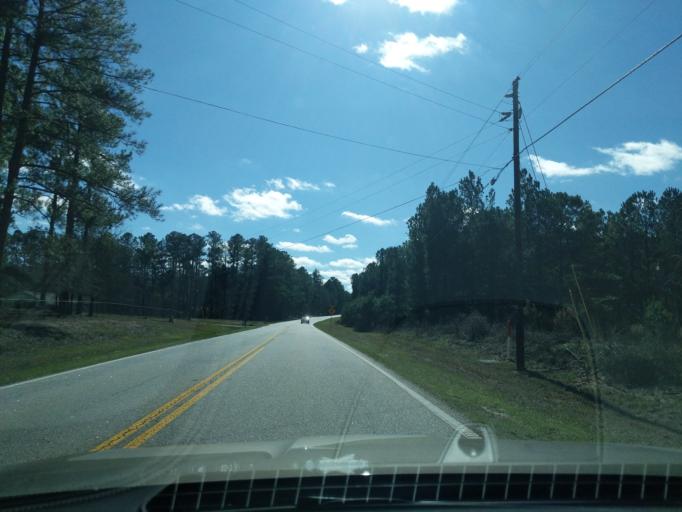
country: US
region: Georgia
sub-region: Columbia County
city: Grovetown
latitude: 33.5226
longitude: -82.2027
